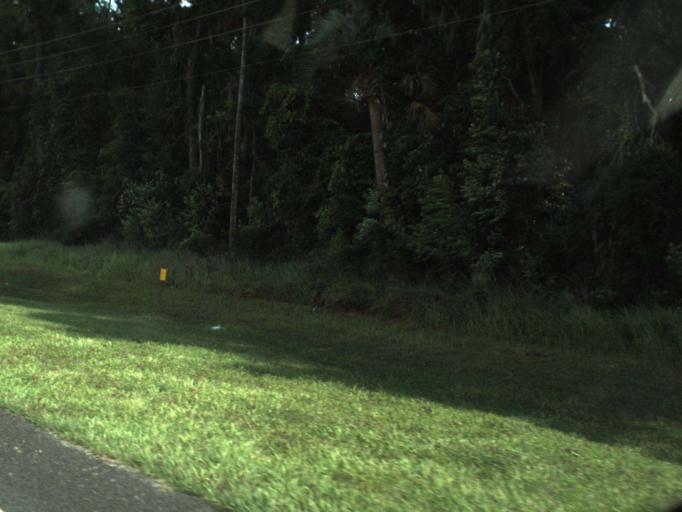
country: US
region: Florida
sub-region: Marion County
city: Ocala
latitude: 29.1519
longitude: -82.0777
